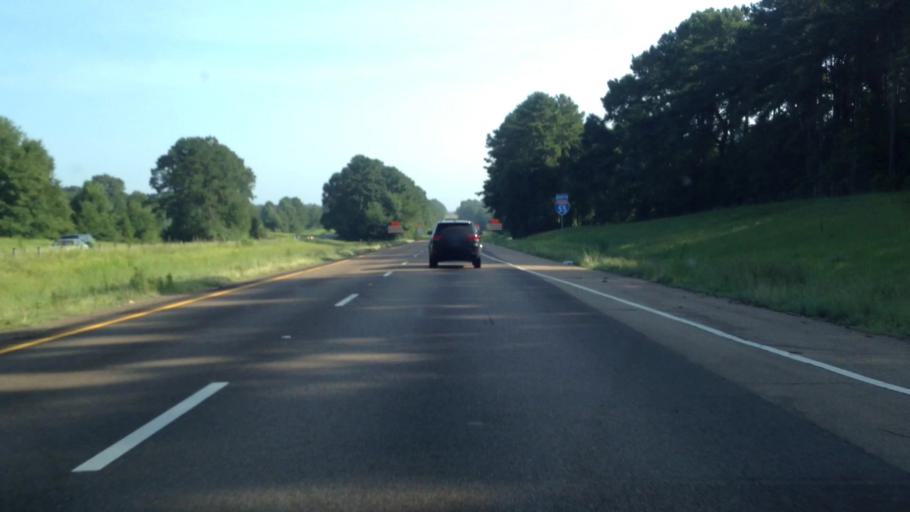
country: US
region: Mississippi
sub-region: Pike County
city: Summit
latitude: 31.2938
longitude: -90.4783
